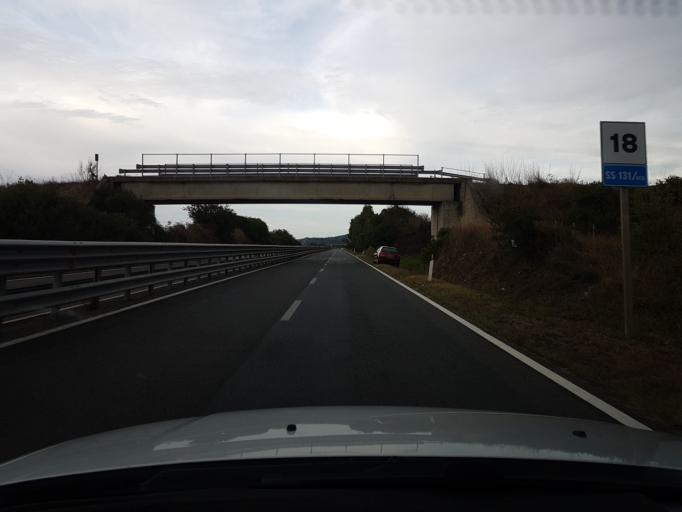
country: IT
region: Sardinia
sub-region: Provincia di Oristano
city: Sedilo
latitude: 40.1857
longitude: 8.9693
